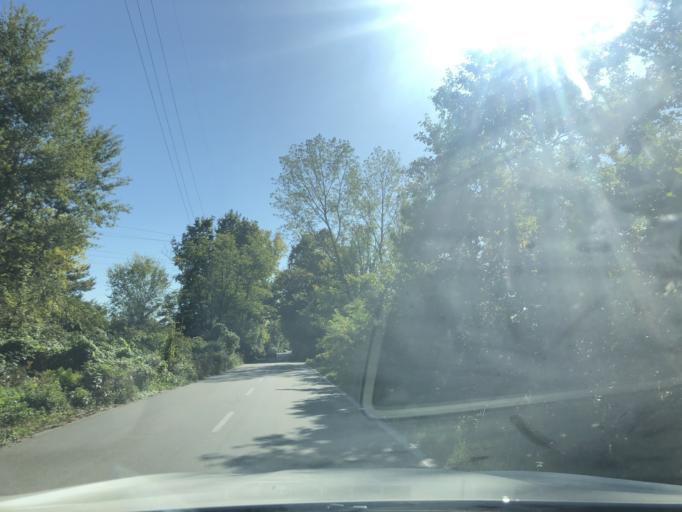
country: IT
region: Lombardy
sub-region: Provincia di Monza e Brianza
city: Villaggio del Sole
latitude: 45.6271
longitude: 9.1183
